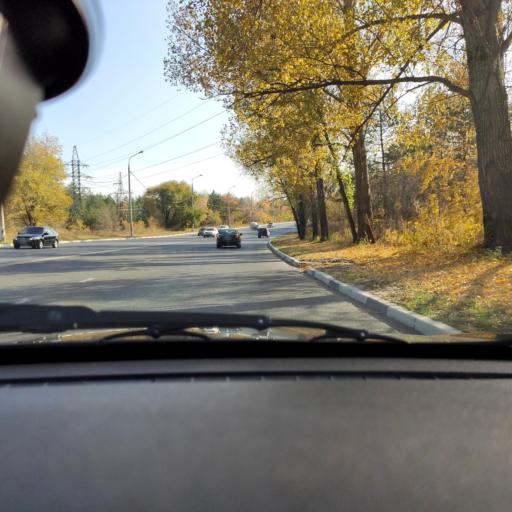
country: RU
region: Samara
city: Zhigulevsk
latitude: 53.5028
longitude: 49.4708
